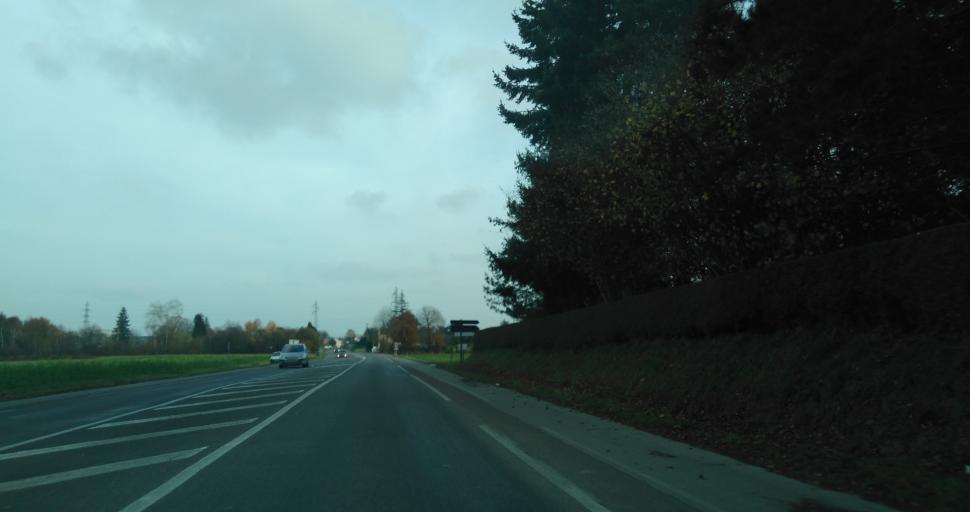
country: FR
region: Brittany
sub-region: Departement d'Ille-et-Vilaine
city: Vezin-le-Coquet
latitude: 48.1181
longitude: -1.7392
